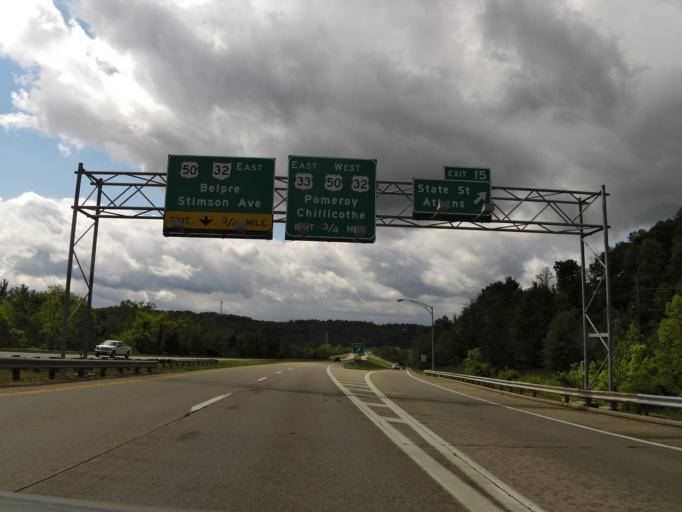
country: US
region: Ohio
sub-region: Athens County
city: Athens
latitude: 39.3428
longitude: -82.0812
